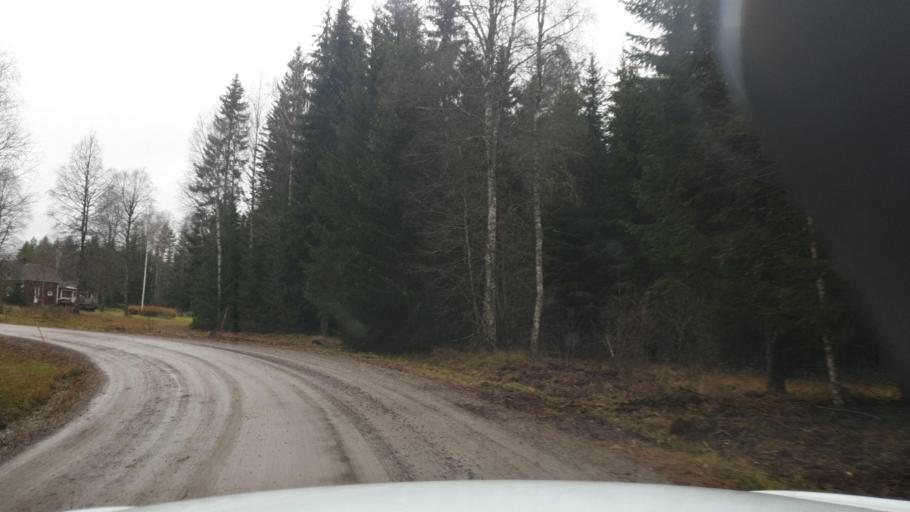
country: SE
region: Vaermland
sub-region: Arvika Kommun
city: Arvika
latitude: 59.8635
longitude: 12.6243
